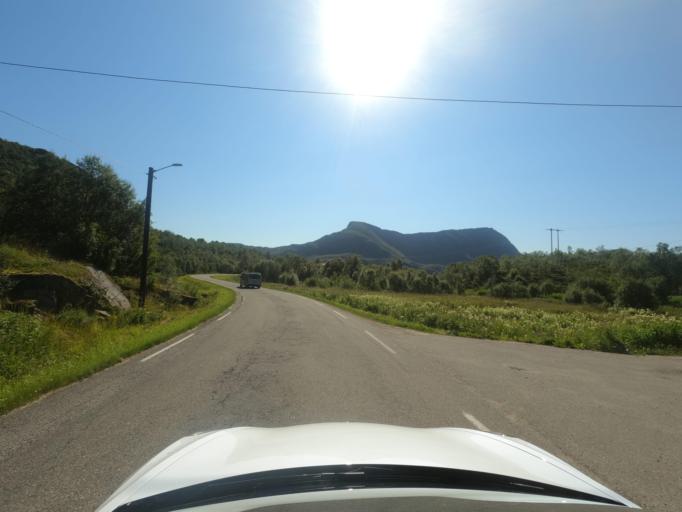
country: NO
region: Nordland
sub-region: Hadsel
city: Stokmarknes
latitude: 68.3085
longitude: 14.9939
